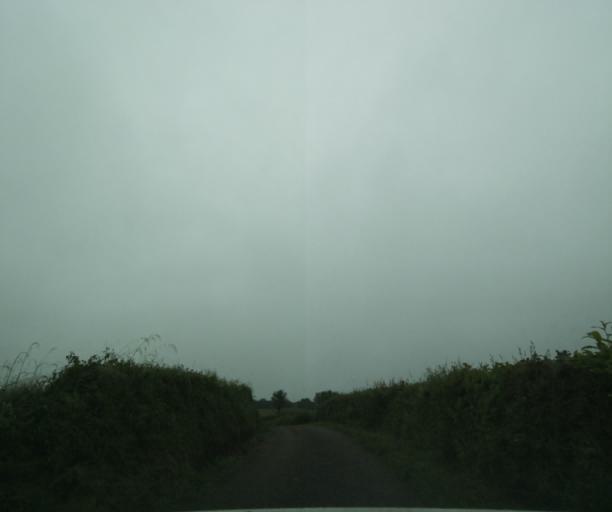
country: FR
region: Bourgogne
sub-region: Departement de Saone-et-Loire
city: Charolles
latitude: 46.4181
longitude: 4.3759
